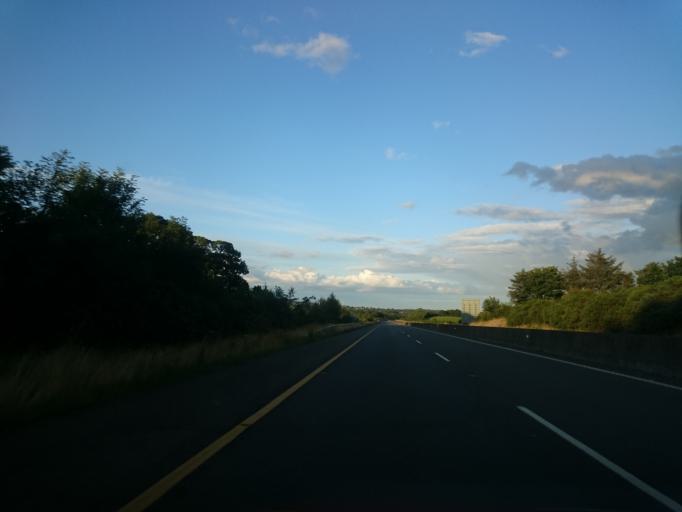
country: IE
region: Leinster
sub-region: Loch Garman
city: Gorey
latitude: 52.6341
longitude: -6.3615
